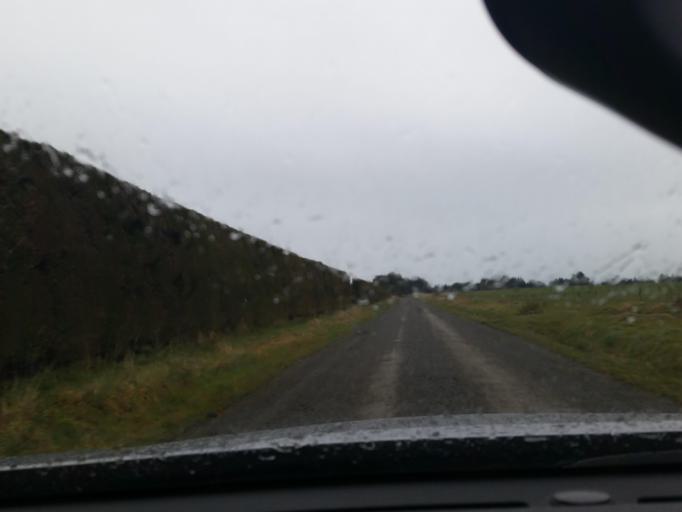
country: NZ
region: Southland
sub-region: Southland District
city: Riverton
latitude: -46.2108
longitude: 168.0785
